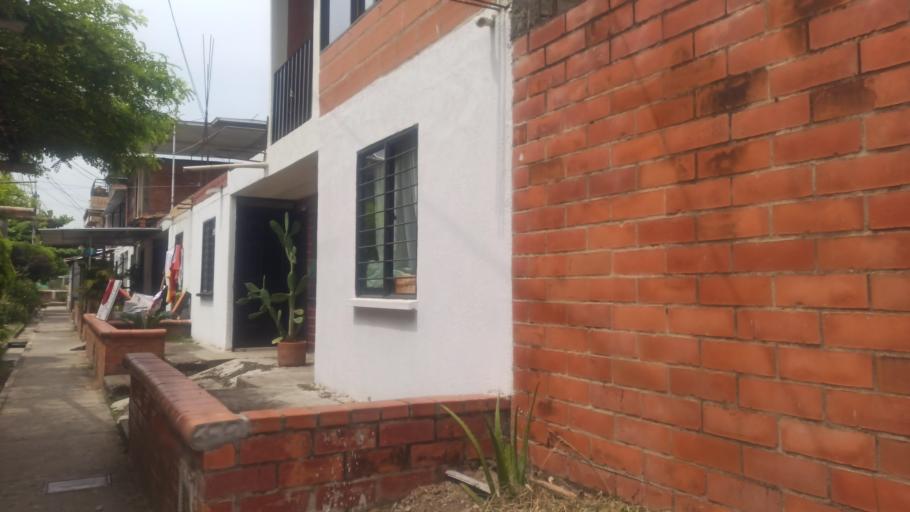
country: CO
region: Valle del Cauca
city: Jamundi
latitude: 3.2353
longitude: -76.5095
